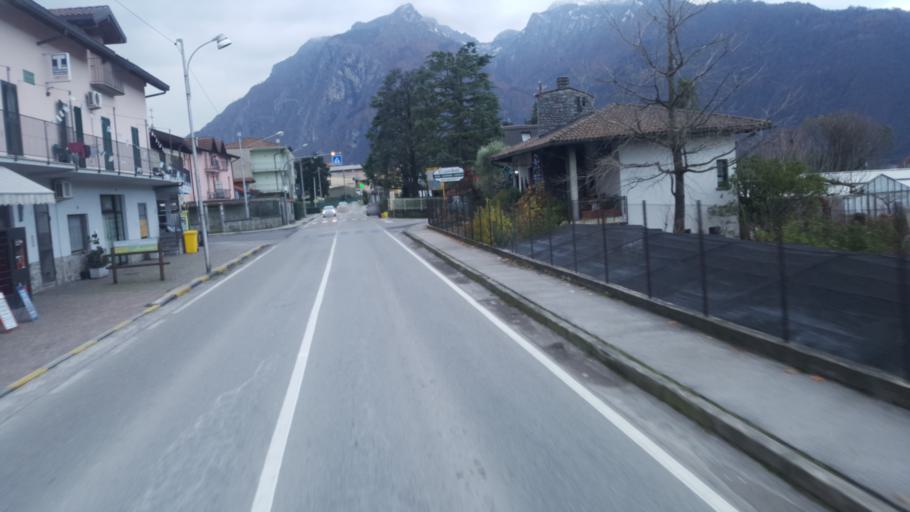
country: IT
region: Lombardy
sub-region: Provincia di Lecco
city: Abbadia Lariana
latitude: 45.9032
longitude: 9.3317
